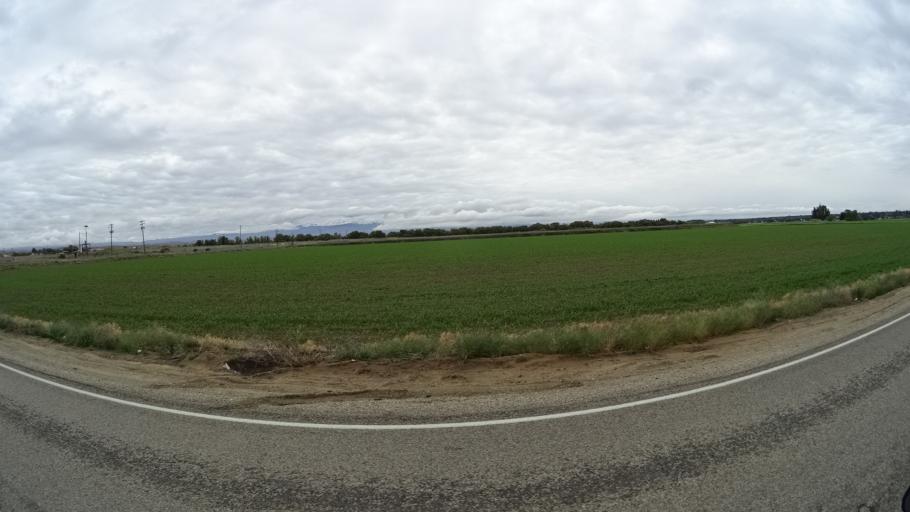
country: US
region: Idaho
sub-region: Ada County
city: Star
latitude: 43.7128
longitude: -116.4434
